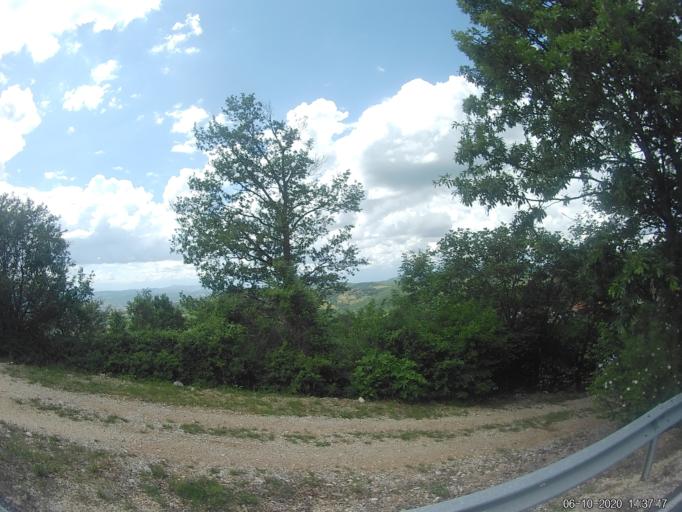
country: XK
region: Prizren
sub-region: Komuna e Therandes
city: Budakovo
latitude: 42.4078
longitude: 20.9398
